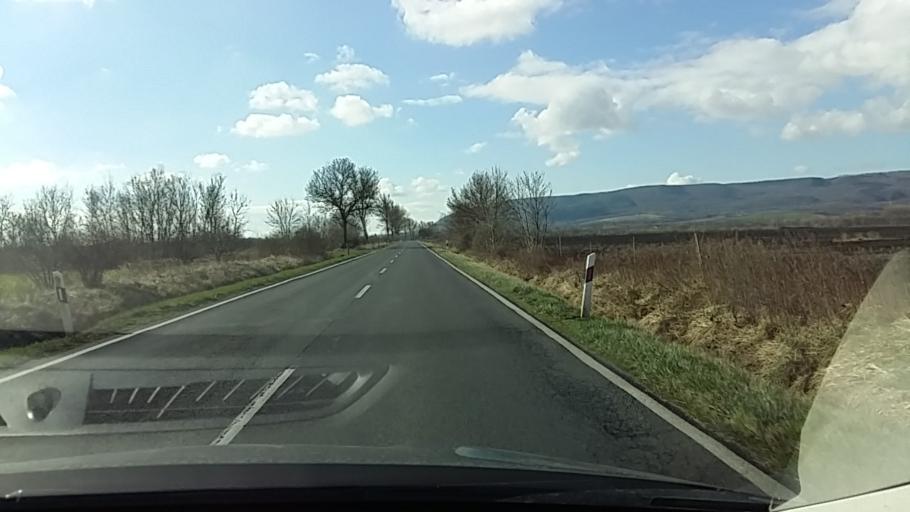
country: HU
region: Veszprem
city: Tapolca
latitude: 46.8643
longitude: 17.3848
